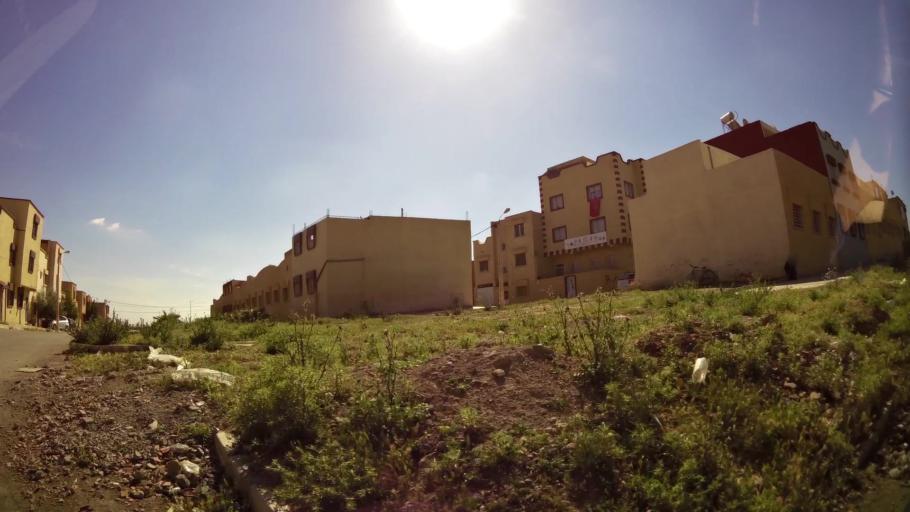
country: MA
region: Oriental
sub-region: Oujda-Angad
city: Oujda
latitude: 34.6537
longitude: -1.9492
